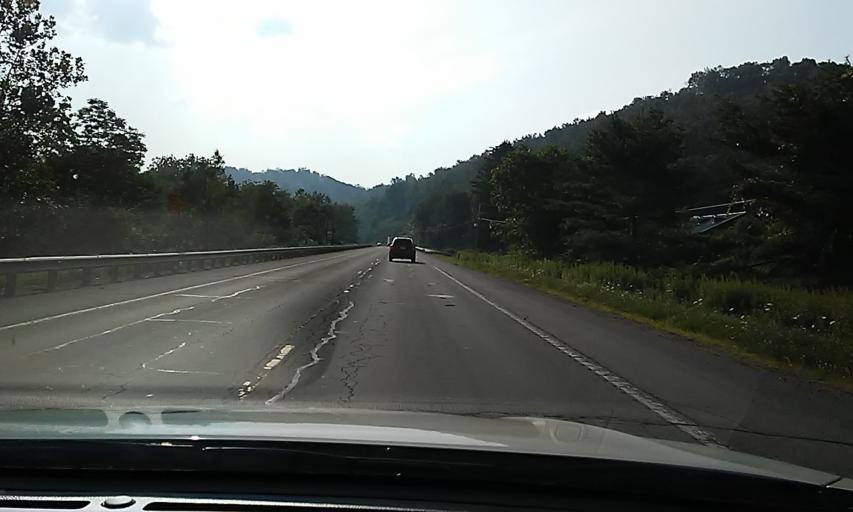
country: US
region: Pennsylvania
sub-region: McKean County
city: Port Allegany
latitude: 41.7910
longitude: -78.1810
